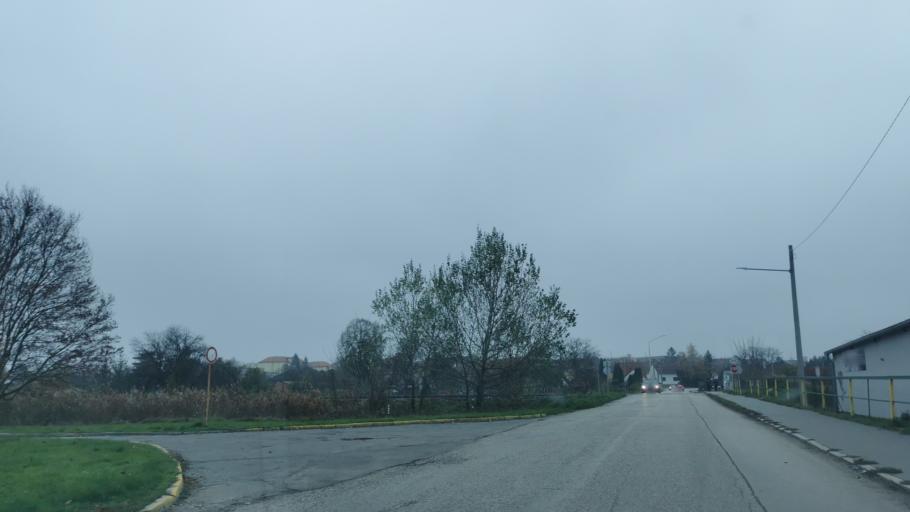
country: SK
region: Trnavsky
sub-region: Okres Skalica
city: Holic
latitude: 48.8219
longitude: 17.1570
